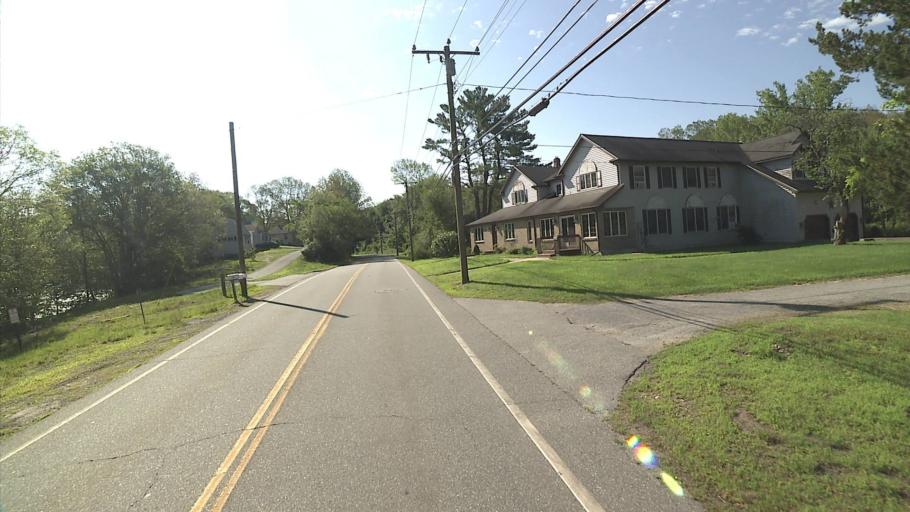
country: US
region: Connecticut
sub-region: New London County
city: Montville Center
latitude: 41.4597
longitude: -72.1477
